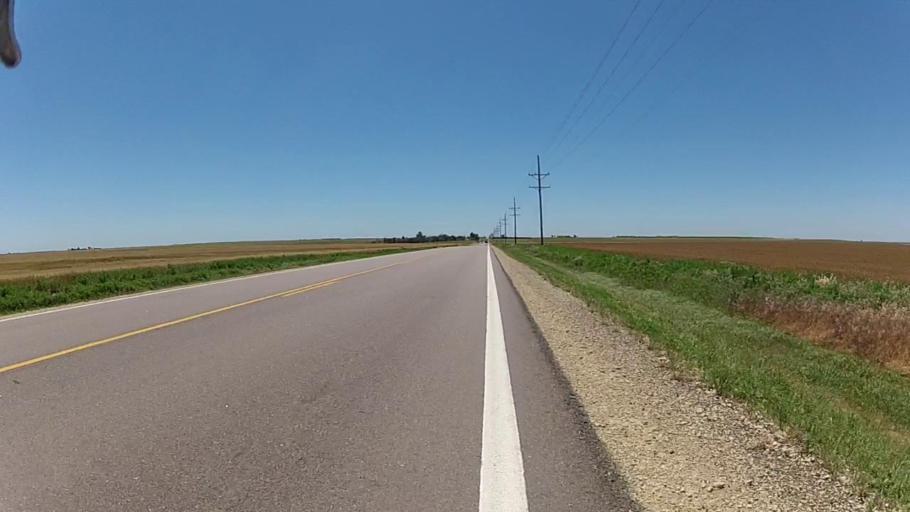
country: US
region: Kansas
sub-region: Kiowa County
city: Greensburg
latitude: 37.5461
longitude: -99.3211
